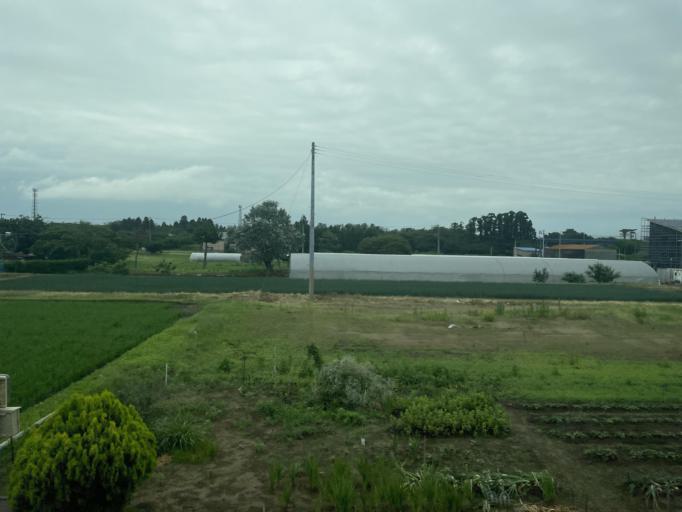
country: JP
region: Akita
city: Tenno
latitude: 39.8891
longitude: 139.9756
